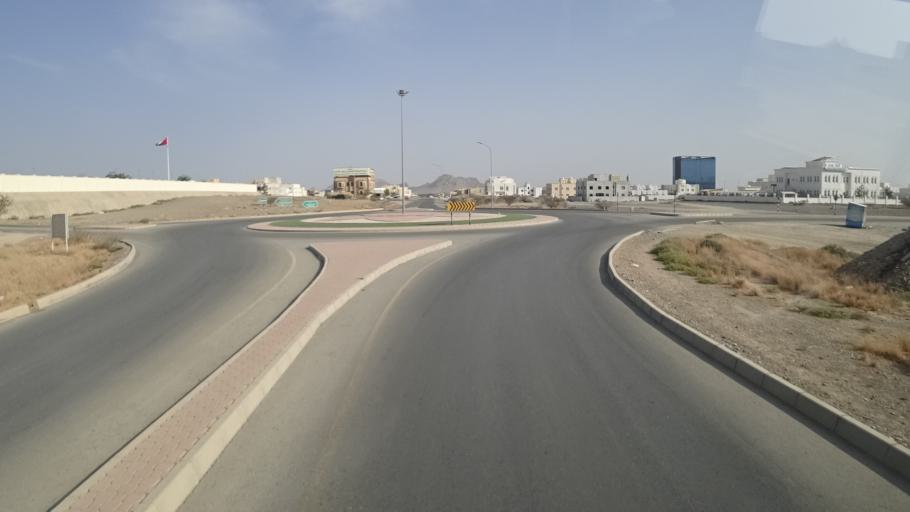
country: OM
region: Muhafazat ad Dakhiliyah
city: Nizwa
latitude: 22.8736
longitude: 57.5420
